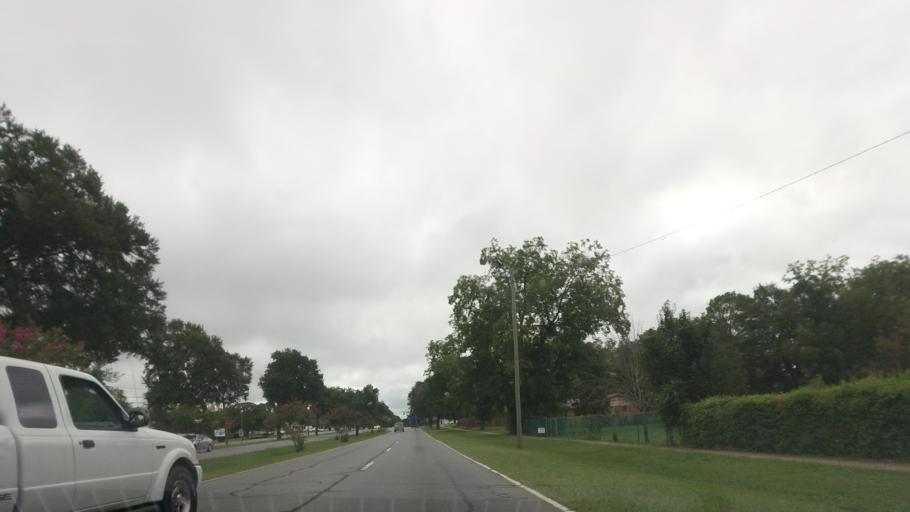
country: US
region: Georgia
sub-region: Laurens County
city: Dublin
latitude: 32.5372
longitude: -82.9363
